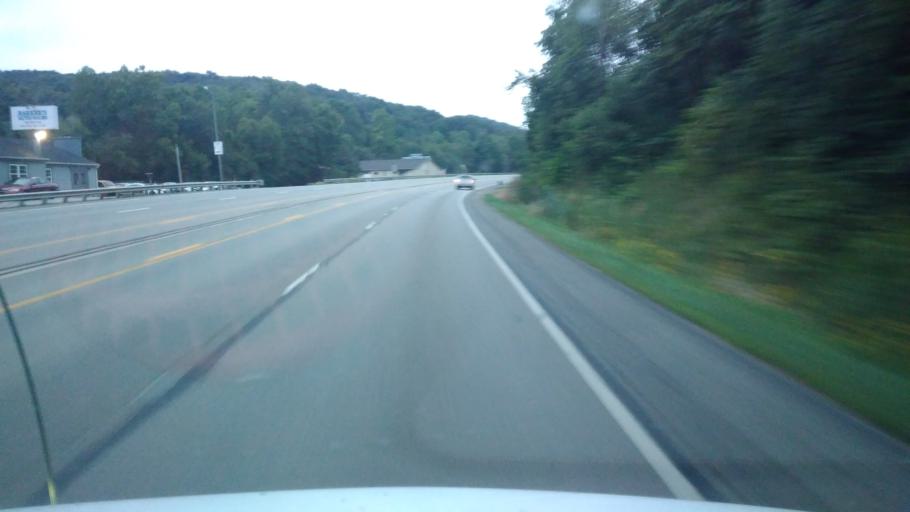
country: US
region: Ohio
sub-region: Pike County
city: Waverly
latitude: 39.2264
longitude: -82.9831
